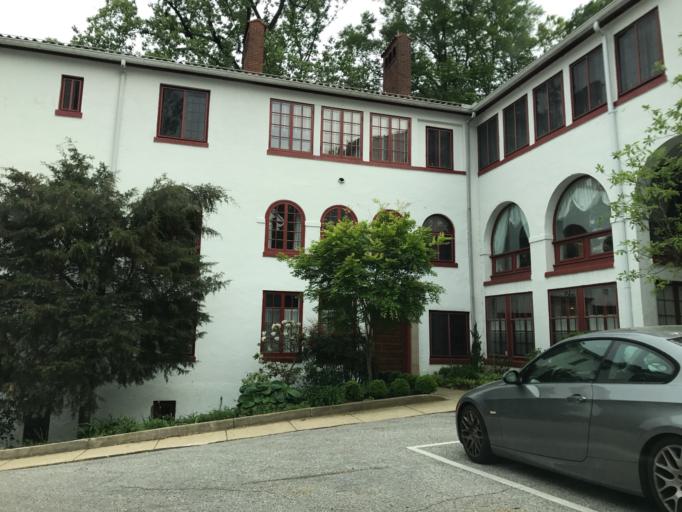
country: US
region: Maryland
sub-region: City of Baltimore
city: Baltimore
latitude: 39.3386
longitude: -76.6238
